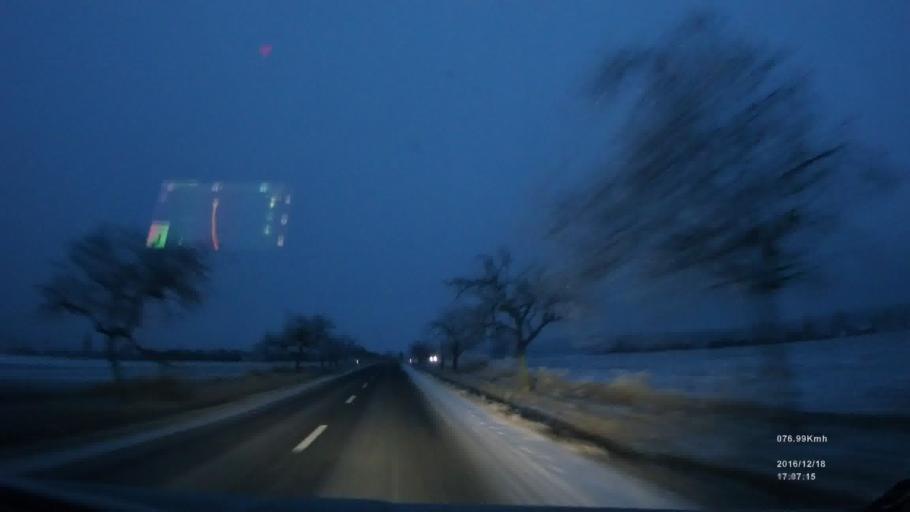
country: SK
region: Presovsky
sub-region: Okres Presov
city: Presov
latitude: 48.8984
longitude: 21.3212
